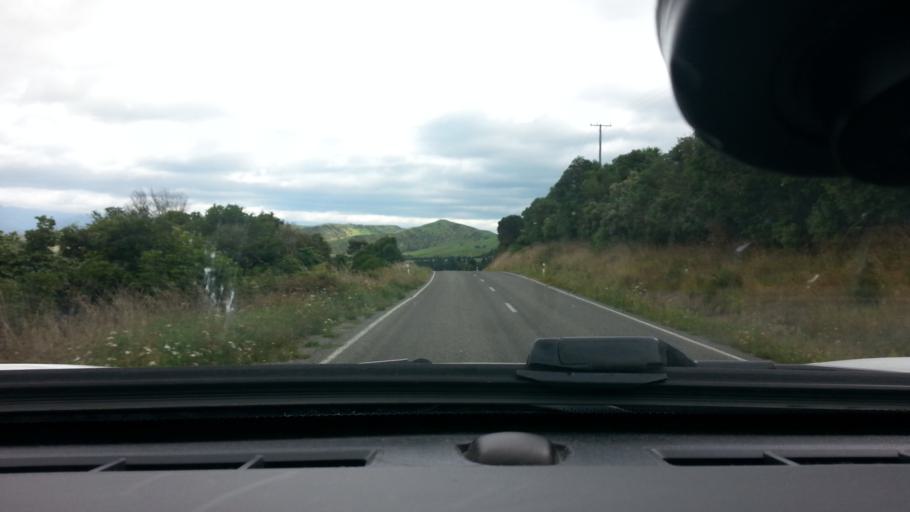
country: NZ
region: Wellington
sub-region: South Wairarapa District
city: Waipawa
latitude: -41.4285
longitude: 175.2262
